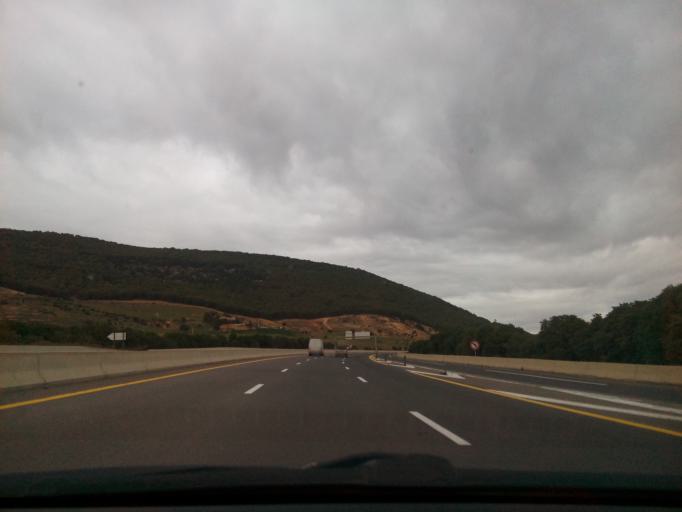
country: DZ
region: Sidi Bel Abbes
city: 'Ain el Berd
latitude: 35.3824
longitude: -0.5000
